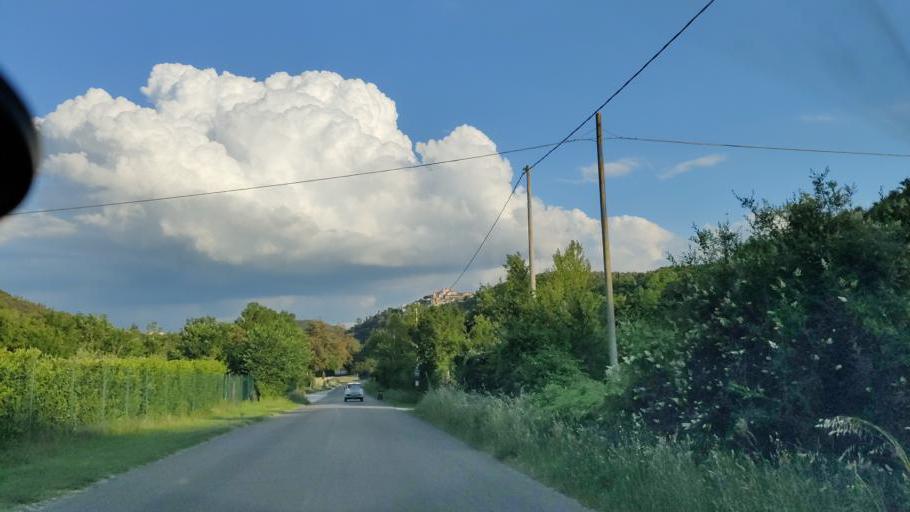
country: IT
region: Umbria
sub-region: Provincia di Terni
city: Amelia
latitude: 42.5697
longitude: 12.4061
